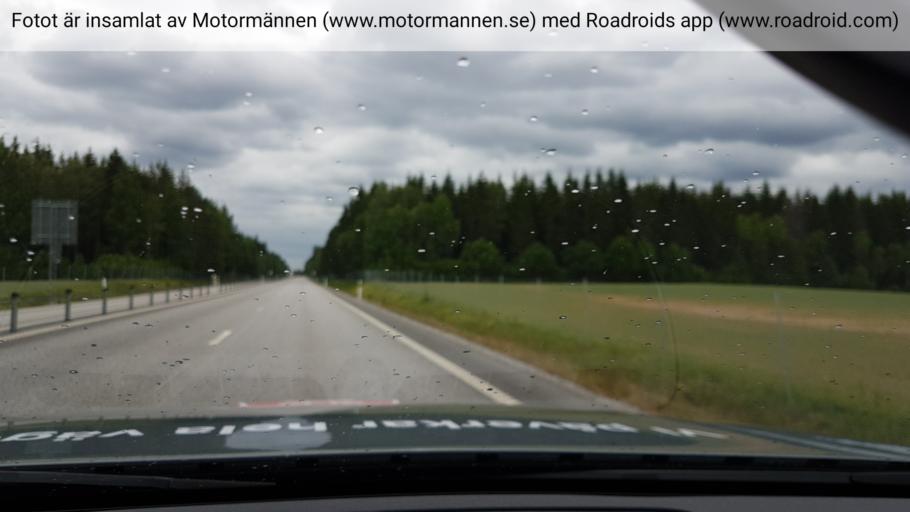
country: SE
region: Vaestmanland
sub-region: Surahammars Kommun
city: Ramnas
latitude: 59.7471
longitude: 16.2259
